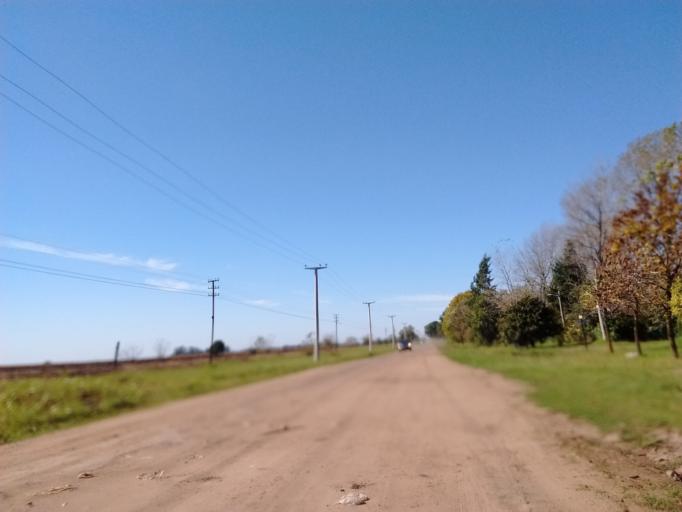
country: AR
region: Santa Fe
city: Funes
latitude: -32.9104
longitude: -60.8490
